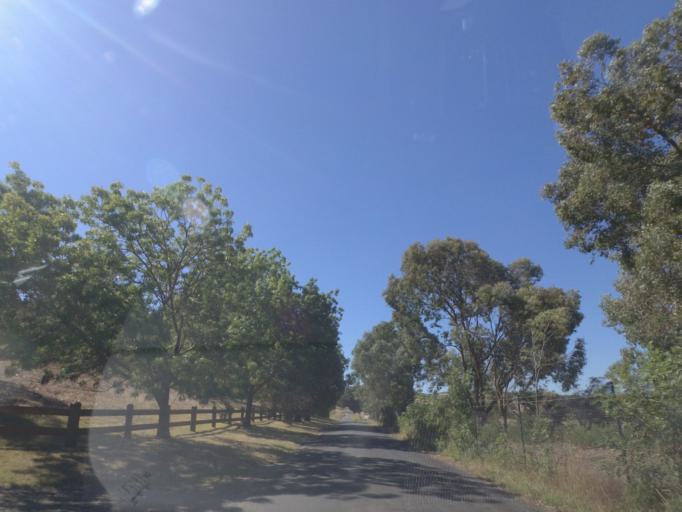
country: AU
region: Victoria
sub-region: Yarra Ranges
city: Chirnside Park
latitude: -37.7182
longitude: 145.2927
